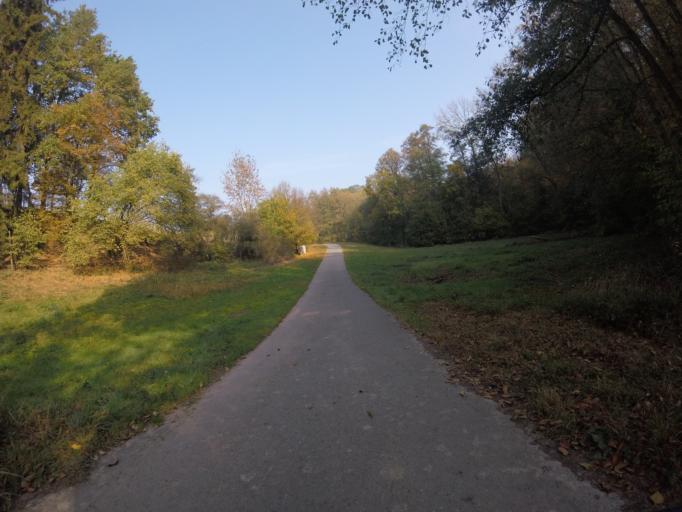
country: DE
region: Baden-Wuerttemberg
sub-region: Regierungsbezirk Stuttgart
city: Mittelschontal
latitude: 48.9451
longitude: 9.3990
